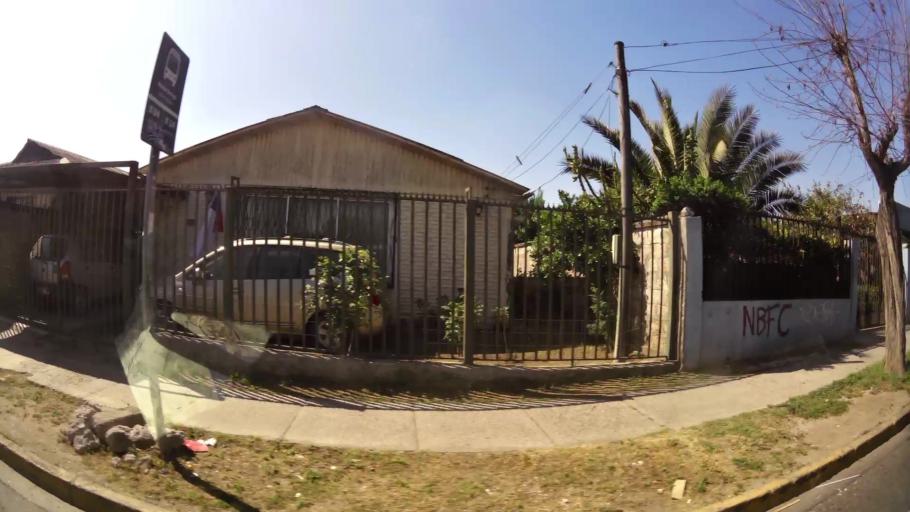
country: CL
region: Santiago Metropolitan
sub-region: Provincia de Santiago
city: Lo Prado
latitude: -33.4993
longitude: -70.7267
